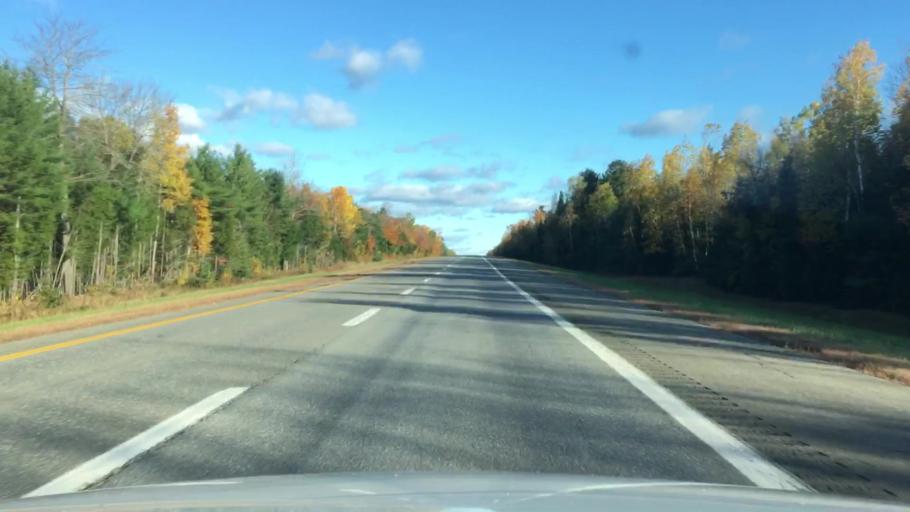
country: US
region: Maine
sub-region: Penobscot County
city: Greenbush
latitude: 45.0657
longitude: -68.6894
